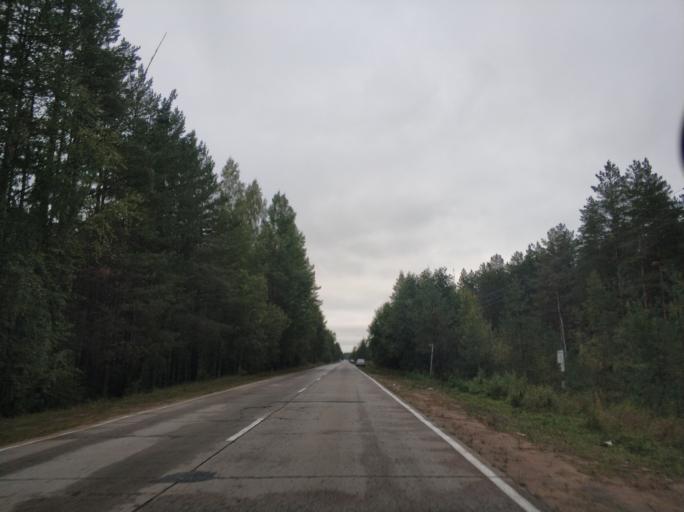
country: RU
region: Leningrad
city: Borisova Griva
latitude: 60.1751
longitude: 30.9193
